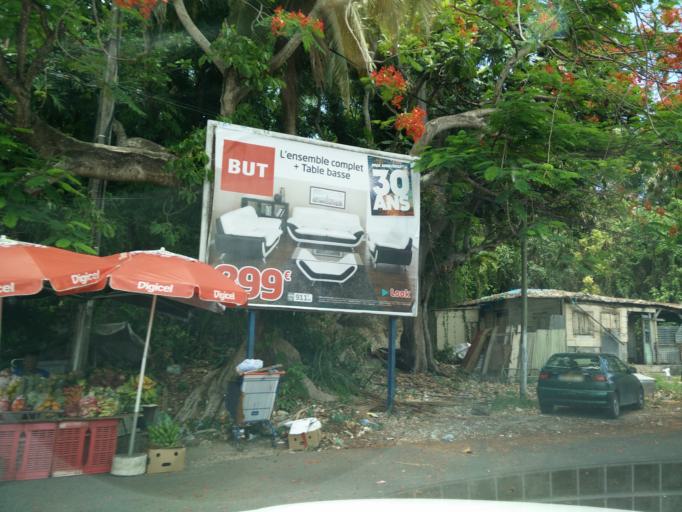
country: GP
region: Guadeloupe
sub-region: Guadeloupe
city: Pointe-a-Pitre
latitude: 16.2231
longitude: -61.5258
